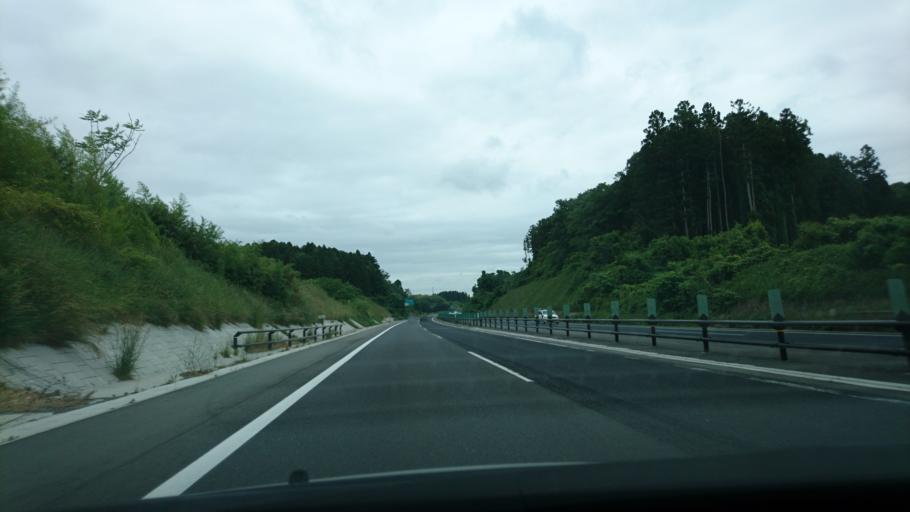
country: JP
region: Miyagi
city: Yamoto
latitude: 38.5502
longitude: 141.2707
